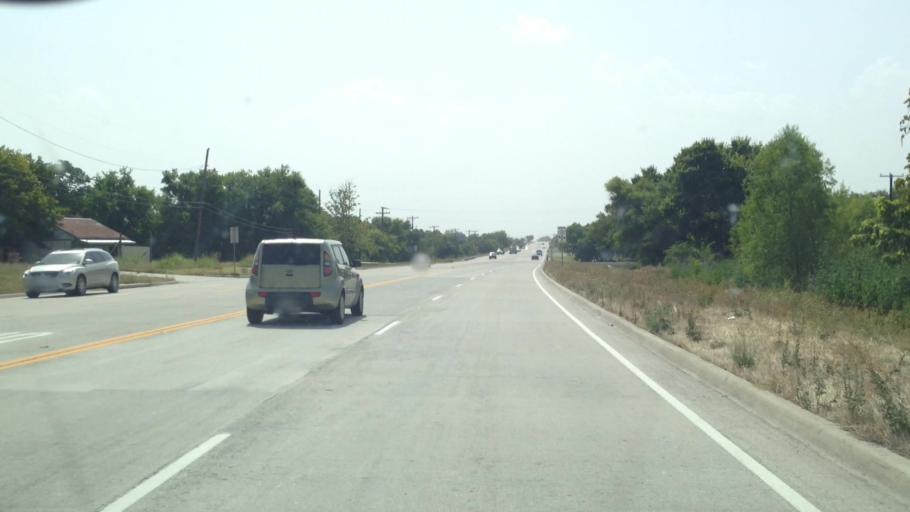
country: US
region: Texas
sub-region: Collin County
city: Farmersville
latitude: 33.1566
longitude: -96.3653
